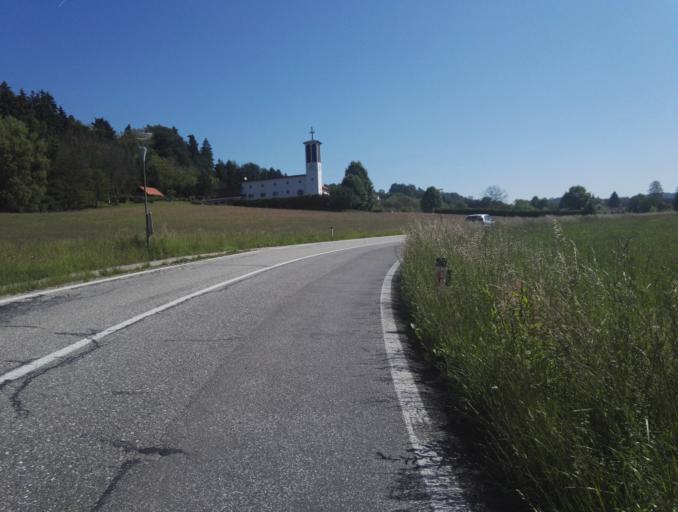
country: AT
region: Styria
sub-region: Politischer Bezirk Graz-Umgebung
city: Hart bei Graz
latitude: 47.0591
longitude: 15.5419
